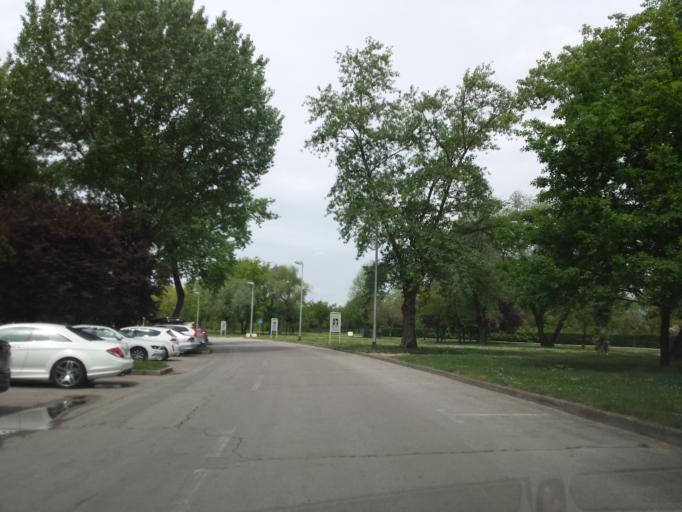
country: HR
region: Grad Zagreb
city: Jankomir
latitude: 45.7805
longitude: 15.9374
